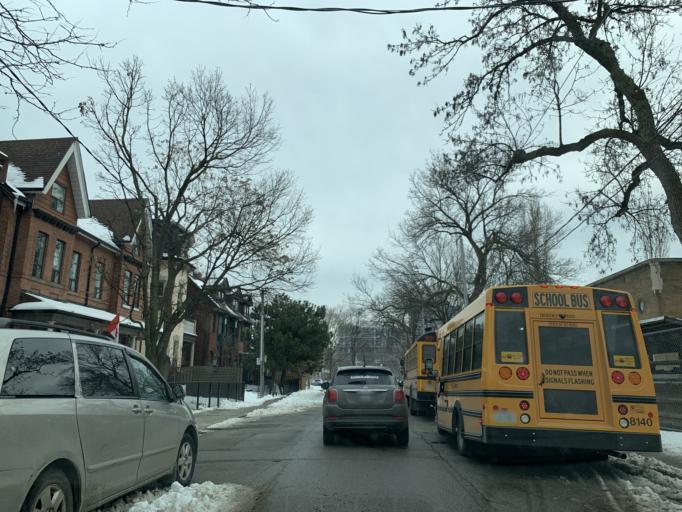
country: CA
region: Ontario
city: Toronto
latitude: 43.6568
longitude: -79.3718
